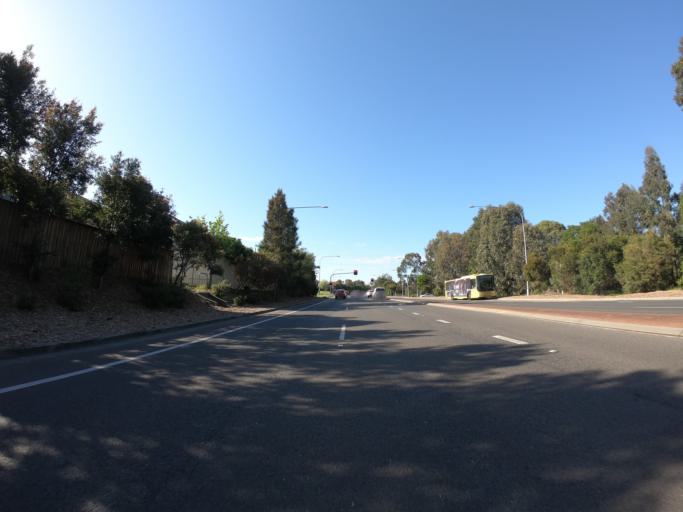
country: AU
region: New South Wales
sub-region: The Hills Shire
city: Glenhaven
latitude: -33.7129
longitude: 150.9744
